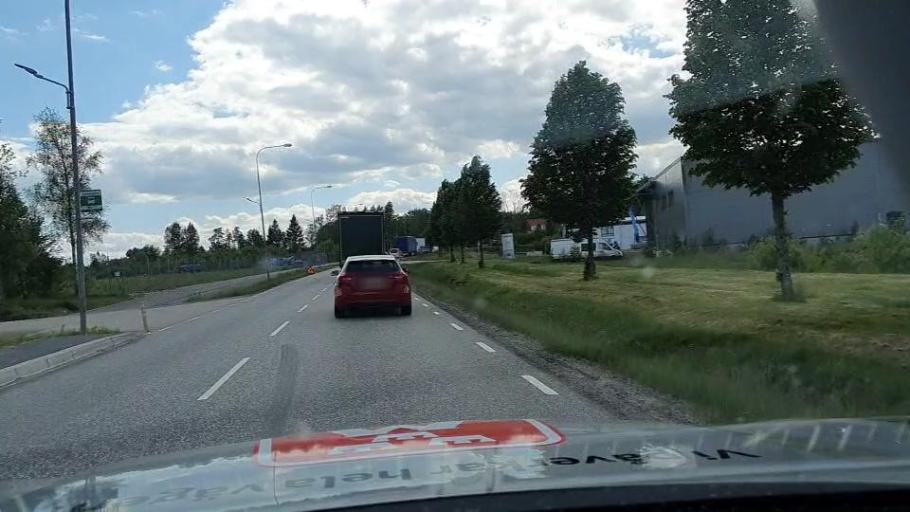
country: SE
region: Kronoberg
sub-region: Ljungby Kommun
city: Ljungby
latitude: 56.8449
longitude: 13.9199
